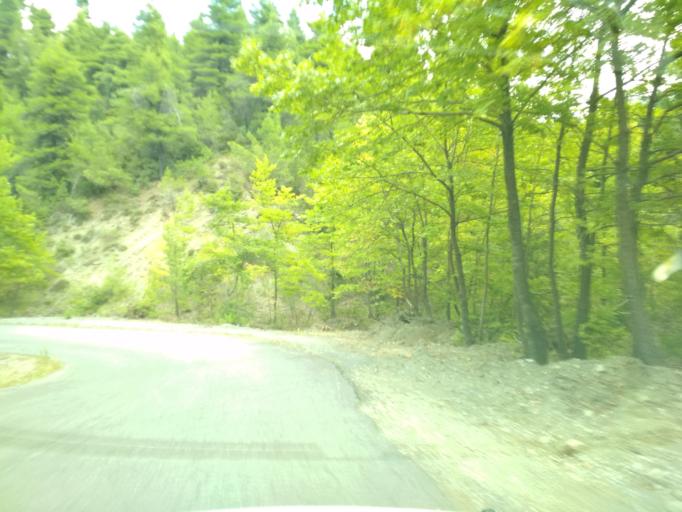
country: GR
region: Central Greece
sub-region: Nomos Evvoias
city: Roviai
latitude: 38.8520
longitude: 23.2860
